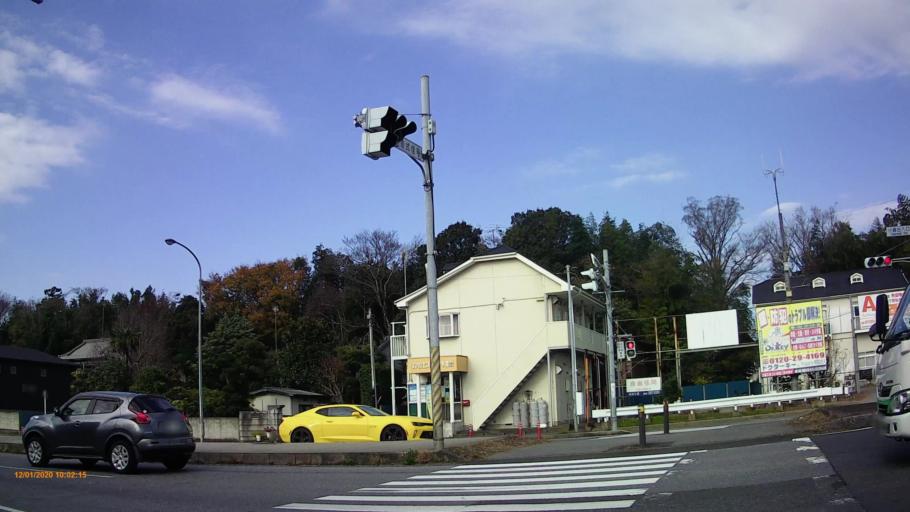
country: JP
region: Chiba
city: Yotsukaido
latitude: 35.6353
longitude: 140.1644
